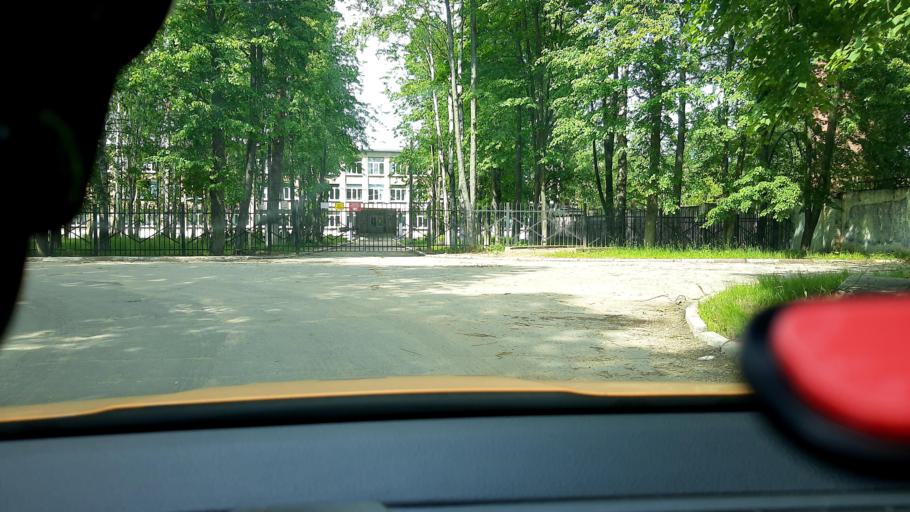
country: RU
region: Moskovskaya
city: Kubinka
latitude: 55.5639
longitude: 36.7036
